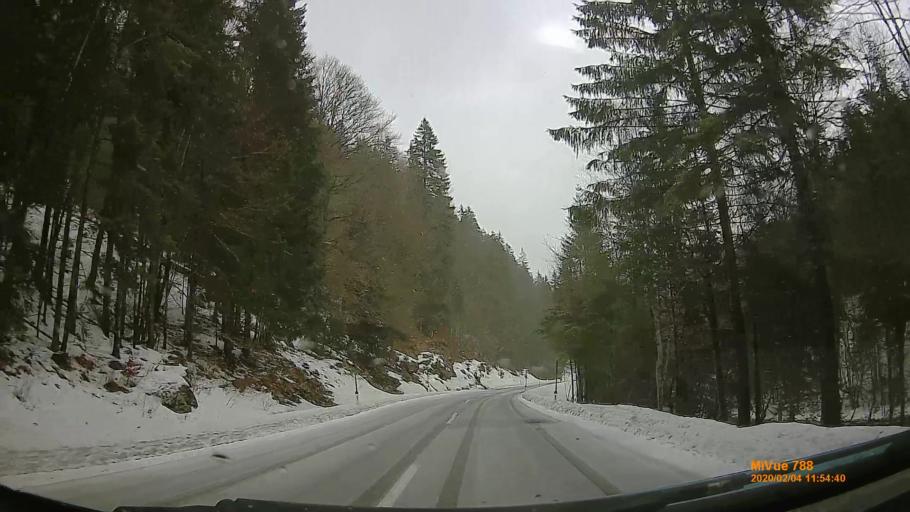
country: AT
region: Styria
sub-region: Politischer Bezirk Bruck-Muerzzuschlag
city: Muerzsteg
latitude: 47.7531
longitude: 15.5032
